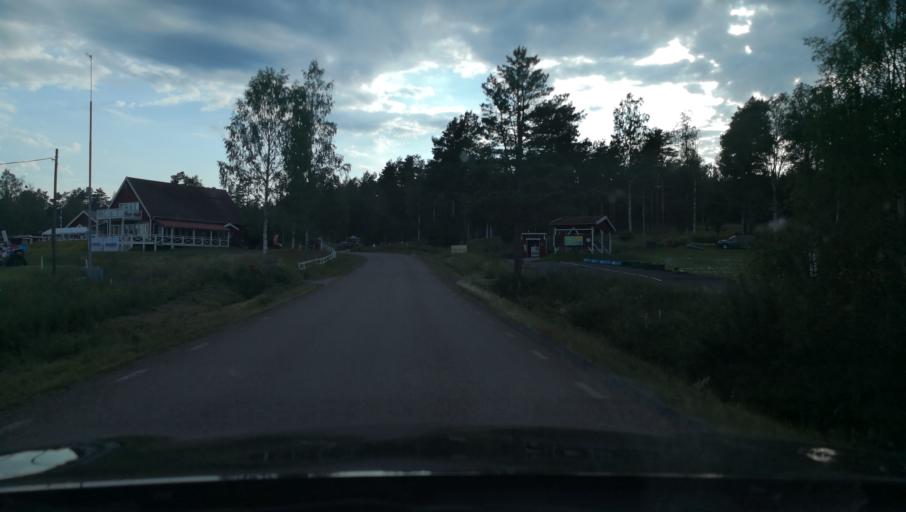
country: SE
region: Dalarna
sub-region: Ludvika Kommun
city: Ludvika
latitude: 60.1165
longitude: 15.2515
